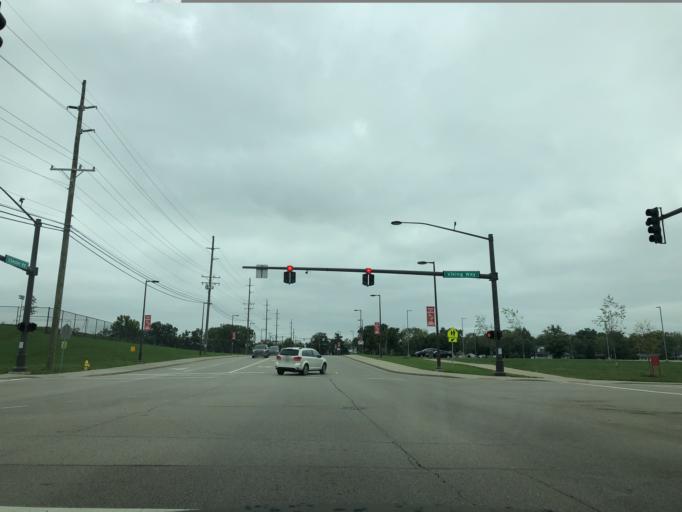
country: US
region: Ohio
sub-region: Hamilton County
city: Glendale
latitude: 39.2734
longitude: -84.4443
